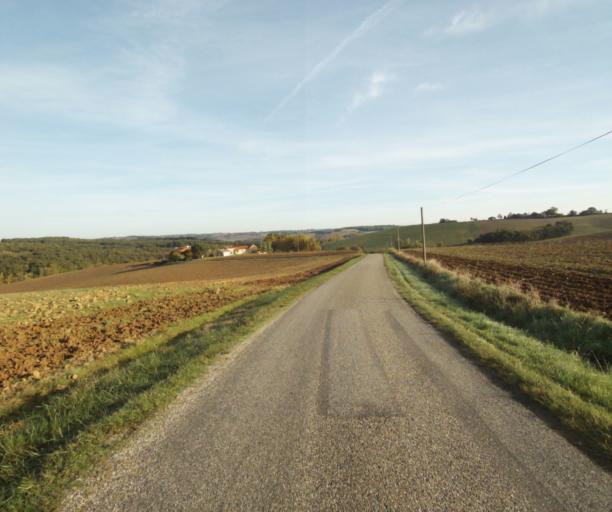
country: FR
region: Midi-Pyrenees
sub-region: Departement du Tarn-et-Garonne
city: Nohic
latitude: 43.9203
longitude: 1.4807
